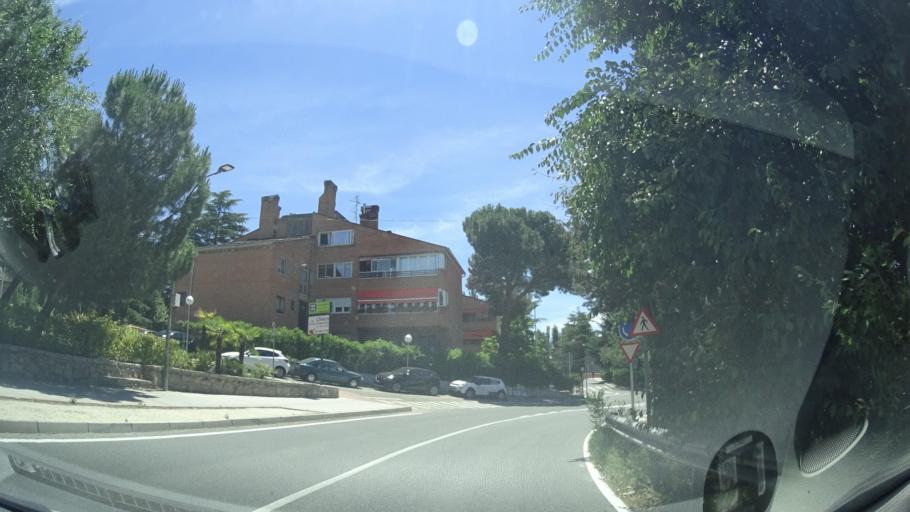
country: ES
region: Madrid
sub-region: Provincia de Madrid
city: Galapagar
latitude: 40.6000
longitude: -3.9825
